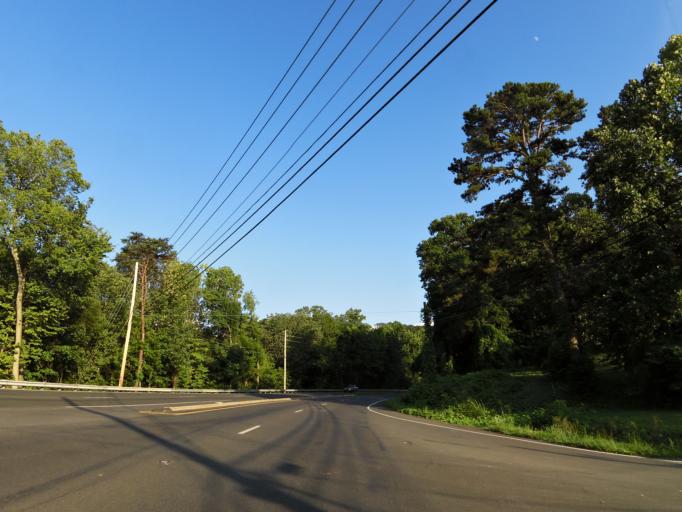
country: US
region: Tennessee
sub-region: Knox County
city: Knoxville
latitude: 36.0136
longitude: -84.0334
